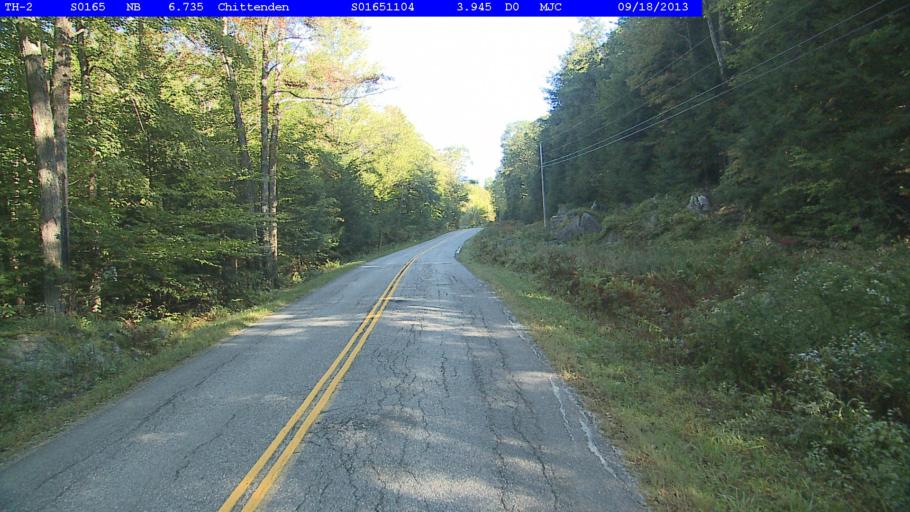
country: US
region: Vermont
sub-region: Rutland County
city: Rutland
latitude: 43.7309
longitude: -72.9707
